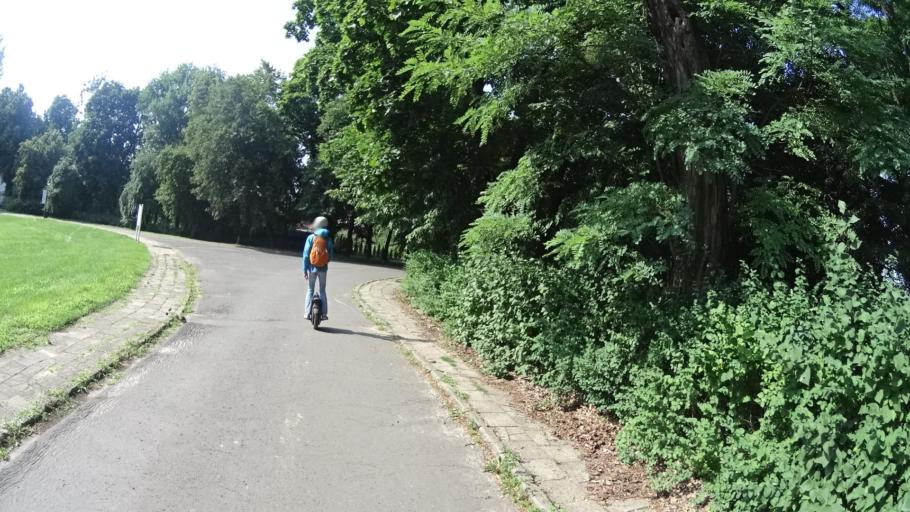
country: PL
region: Masovian Voivodeship
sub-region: Powiat legionowski
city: Jablonna
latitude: 52.3763
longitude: 20.9161
